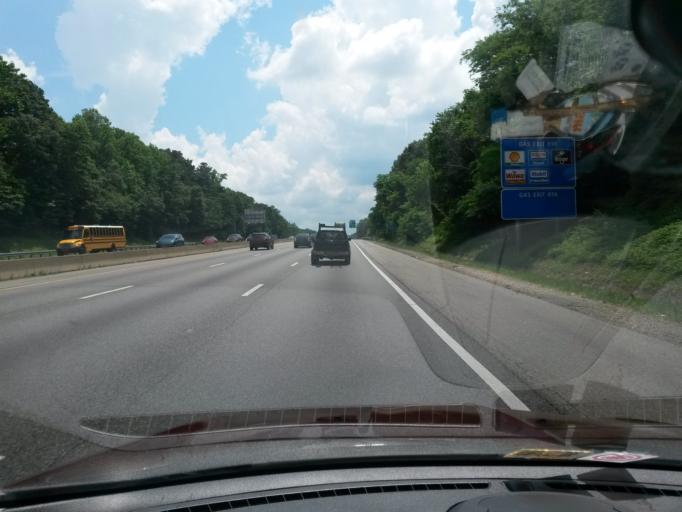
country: US
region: Virginia
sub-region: Chesterfield County
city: Chester
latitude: 37.3635
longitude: -77.4039
